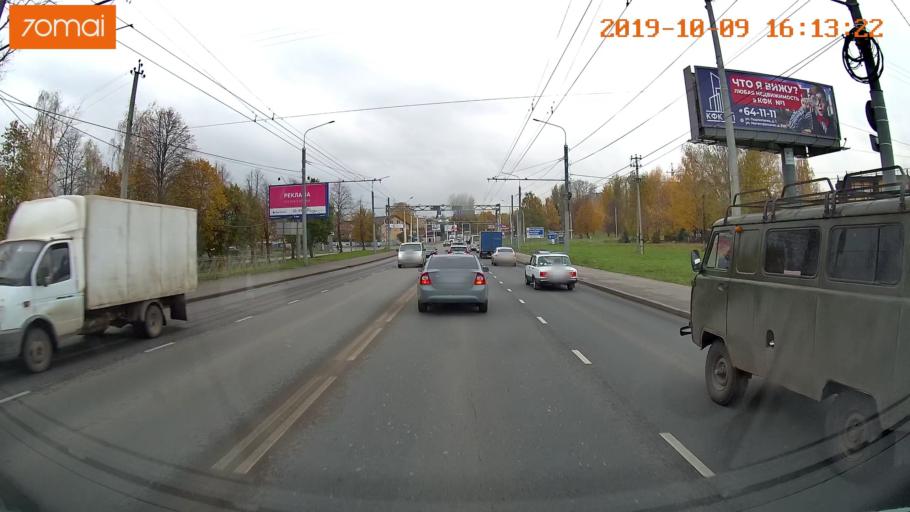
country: RU
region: Kostroma
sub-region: Kostromskoy Rayon
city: Kostroma
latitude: 57.7474
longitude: 40.9309
